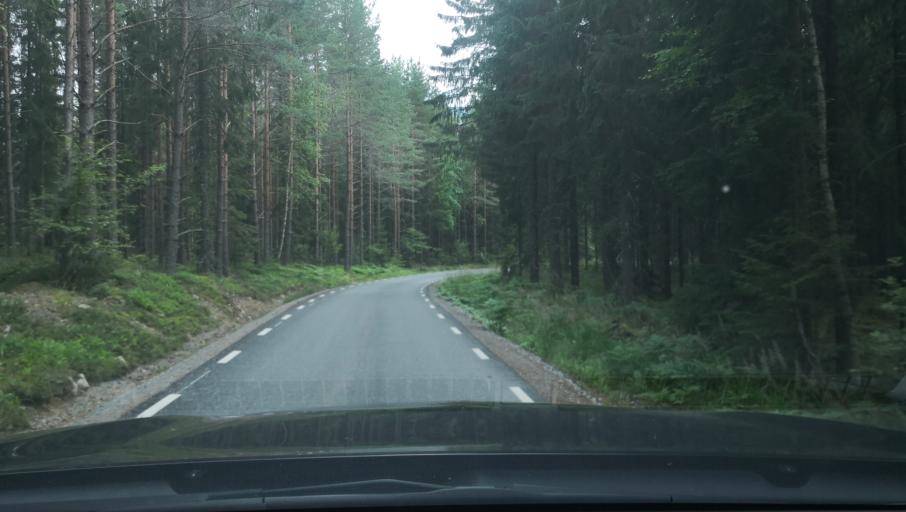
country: SE
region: Vaestmanland
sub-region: Surahammars Kommun
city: Surahammar
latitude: 59.6599
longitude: 16.1317
